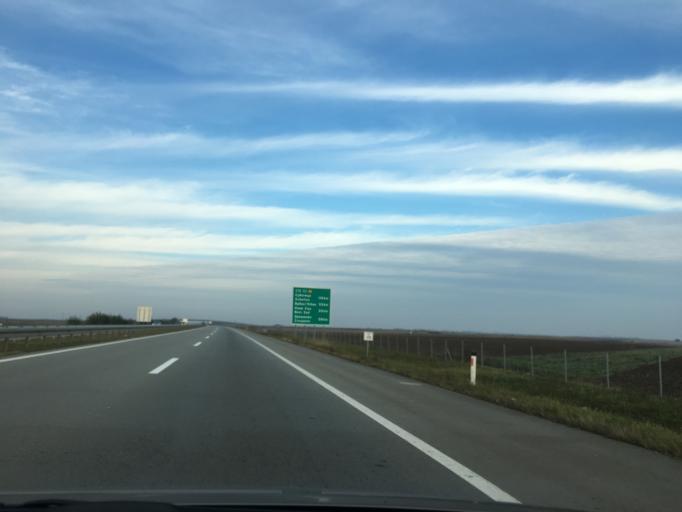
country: RS
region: Autonomna Pokrajina Vojvodina
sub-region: Juznobacki Okrug
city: Kovilj
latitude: 45.2465
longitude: 20.0281
